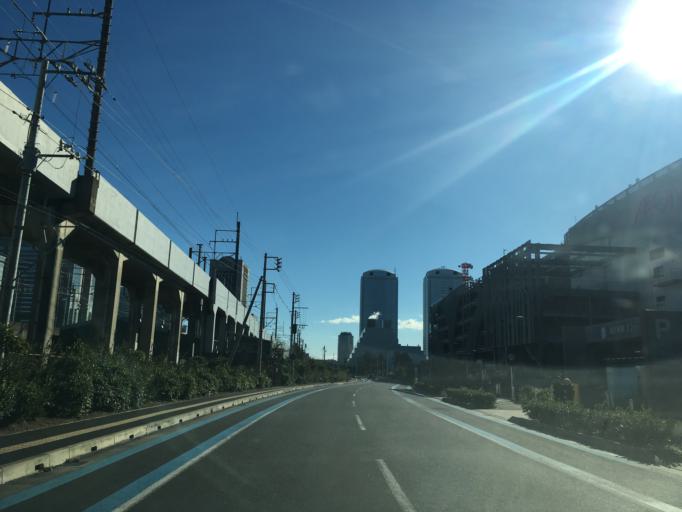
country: JP
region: Chiba
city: Funabashi
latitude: 35.6542
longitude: 140.0323
